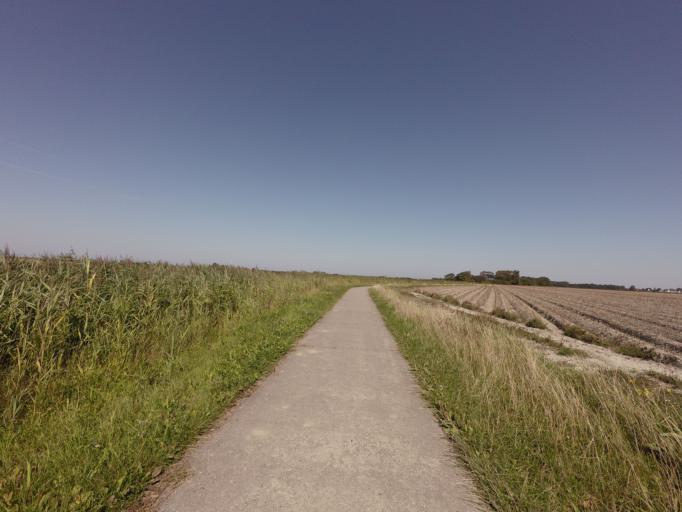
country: NL
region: Friesland
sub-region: Gemeente Dongeradeel
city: Anjum
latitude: 53.3940
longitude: 6.0700
